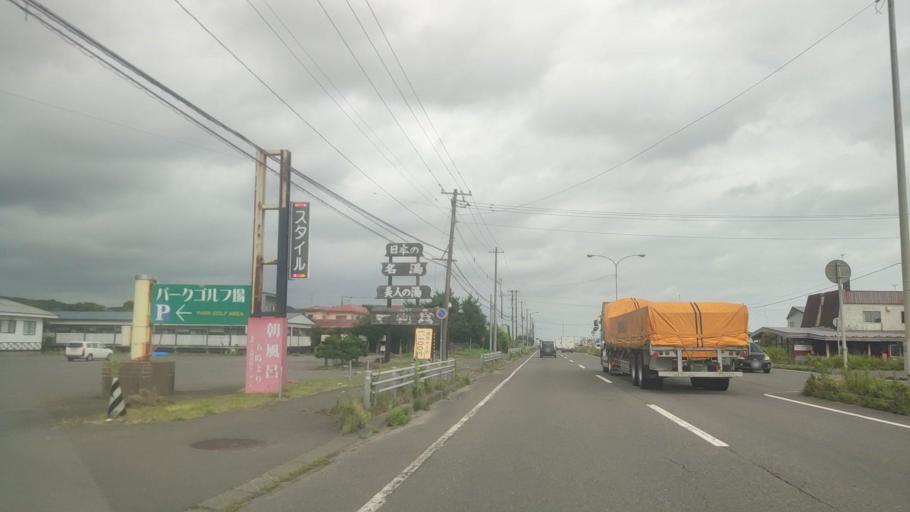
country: JP
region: Hokkaido
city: Shiraoi
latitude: 42.4729
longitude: 141.2341
